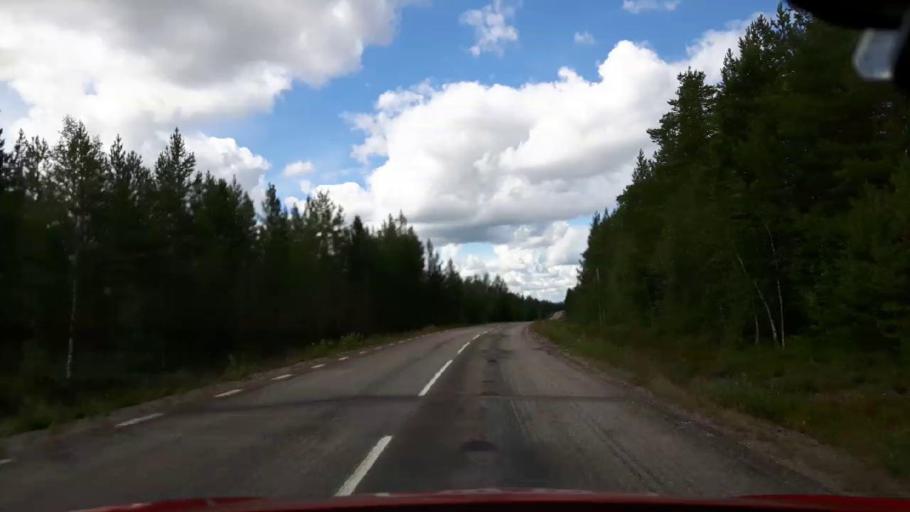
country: SE
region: Jaemtland
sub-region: Harjedalens Kommun
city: Sveg
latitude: 61.8406
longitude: 14.0263
